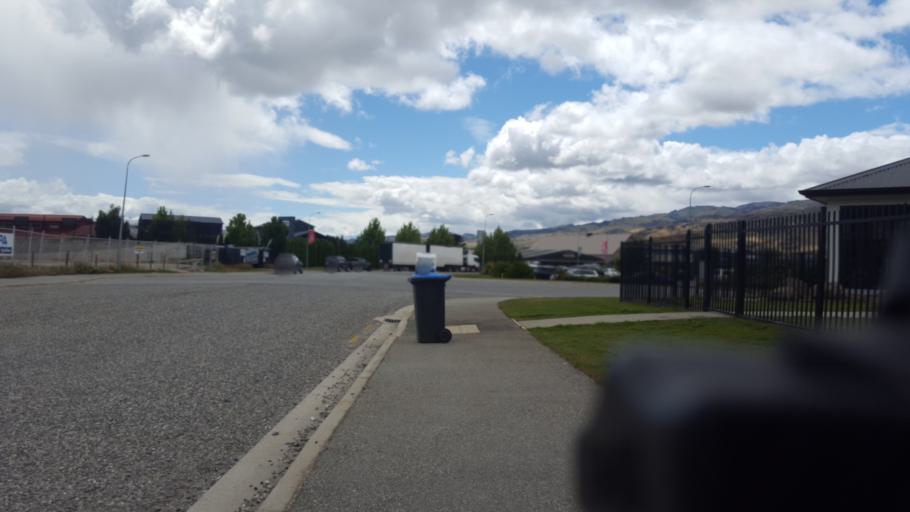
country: NZ
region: Otago
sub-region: Queenstown-Lakes District
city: Wanaka
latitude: -45.0358
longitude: 169.1912
